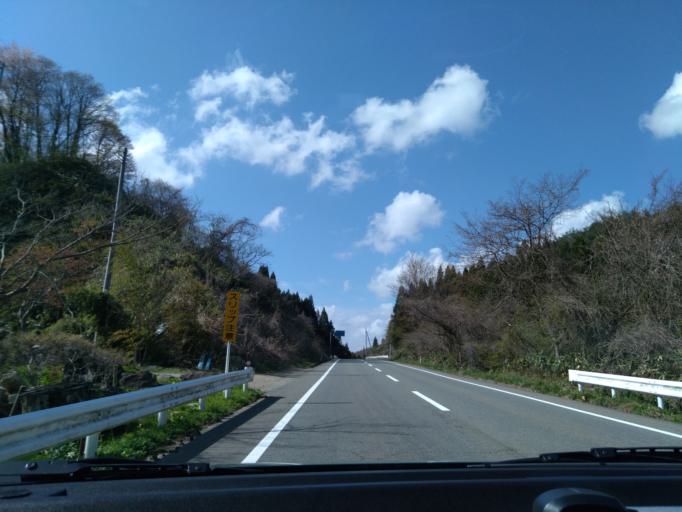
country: JP
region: Akita
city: Akita
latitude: 39.6944
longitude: 140.2219
